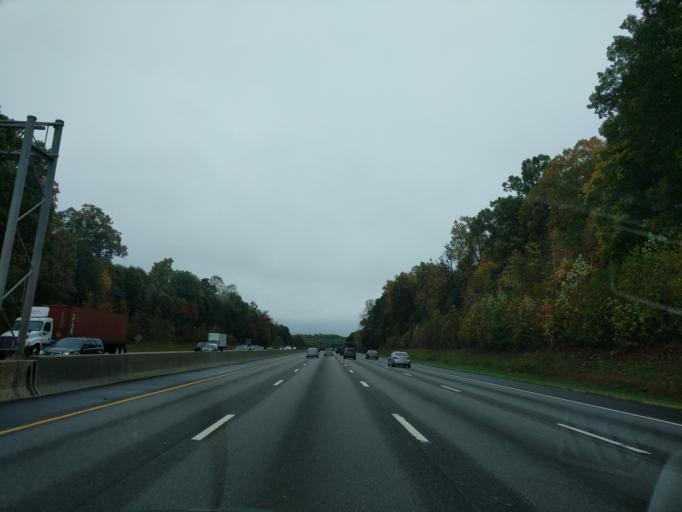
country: US
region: North Carolina
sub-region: Orange County
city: Hillsborough
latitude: 36.0646
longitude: -79.1416
